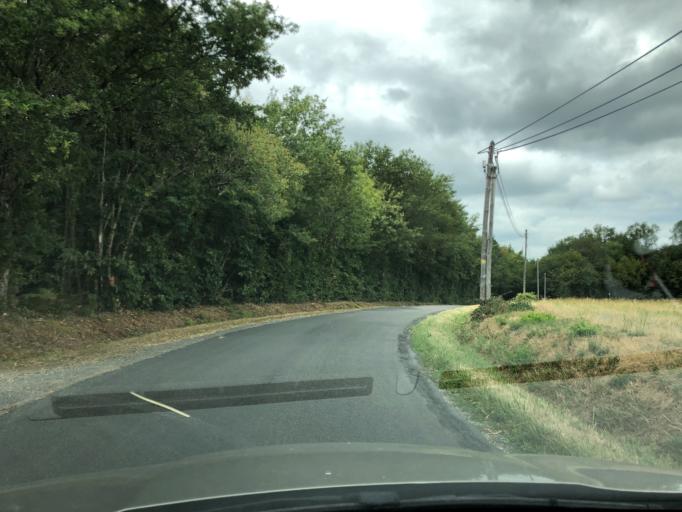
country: FR
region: Centre
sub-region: Departement d'Indre-et-Loire
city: Mazieres-de-Touraine
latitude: 47.3889
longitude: 0.4506
